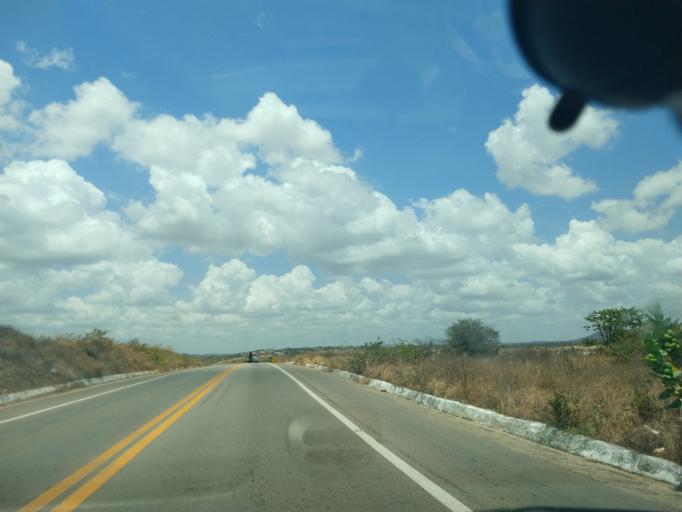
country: BR
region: Rio Grande do Norte
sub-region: Tangara
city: Tangara
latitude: -6.1825
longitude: -35.7736
